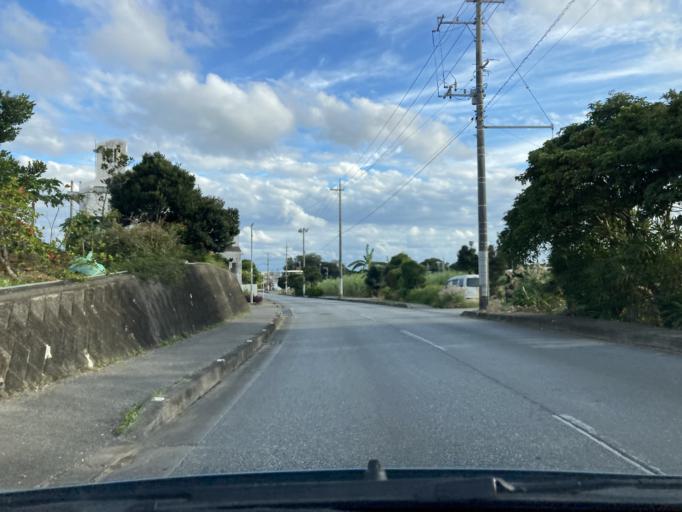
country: JP
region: Okinawa
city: Tomigusuku
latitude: 26.1449
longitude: 127.7454
